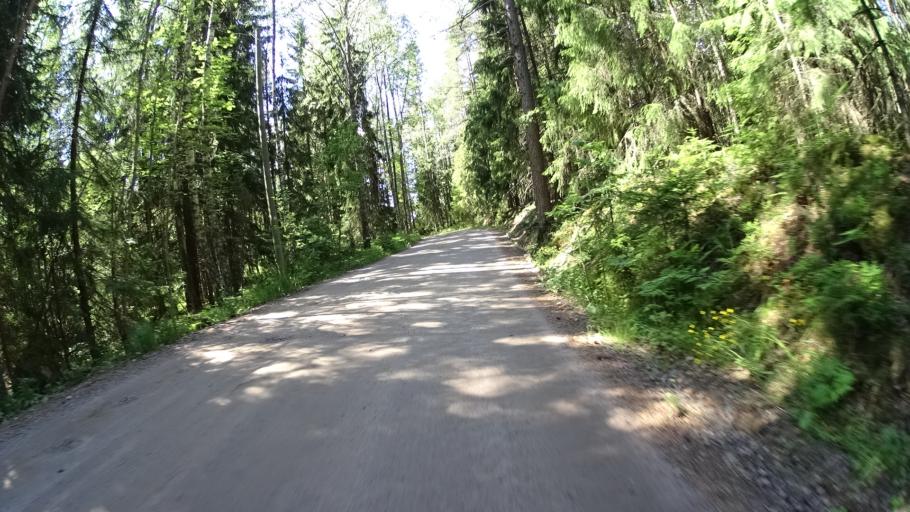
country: FI
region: Uusimaa
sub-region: Helsinki
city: Vihti
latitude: 60.3097
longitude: 24.4383
